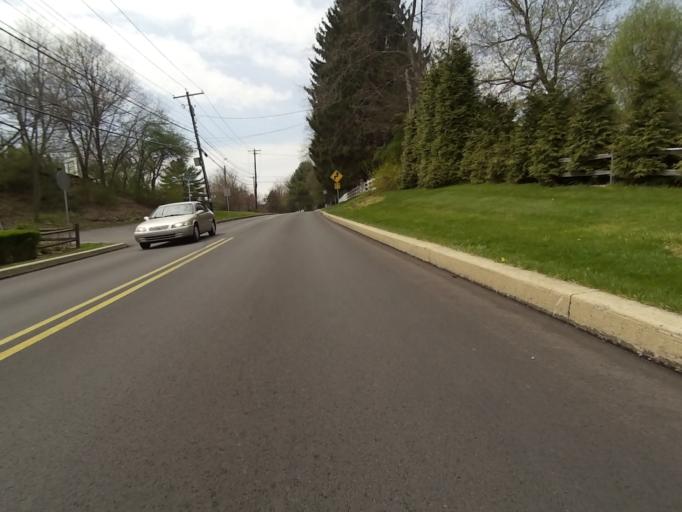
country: US
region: Pennsylvania
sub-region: Centre County
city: Park Forest Village
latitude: 40.7960
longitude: -77.8939
